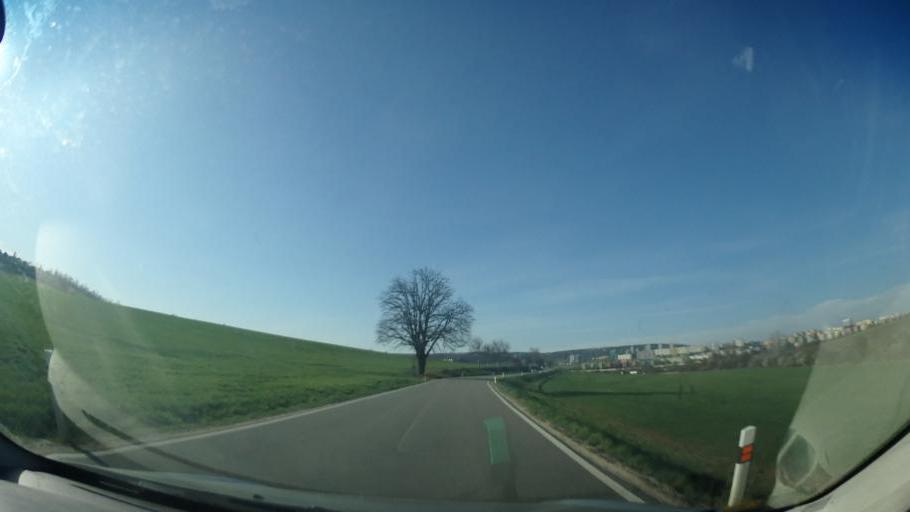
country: CZ
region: South Moravian
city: Ostopovice
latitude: 49.1550
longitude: 16.5537
